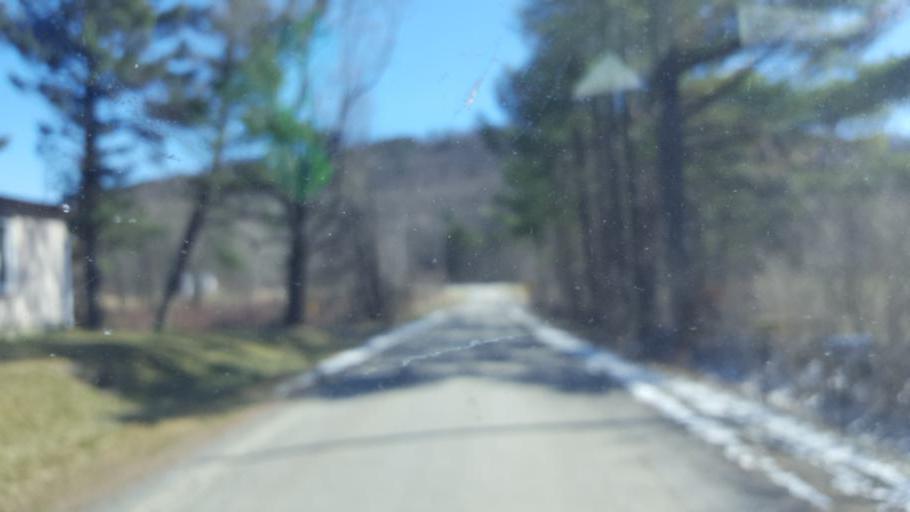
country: US
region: New York
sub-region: Allegany County
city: Wellsville
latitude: 42.0713
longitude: -77.9259
